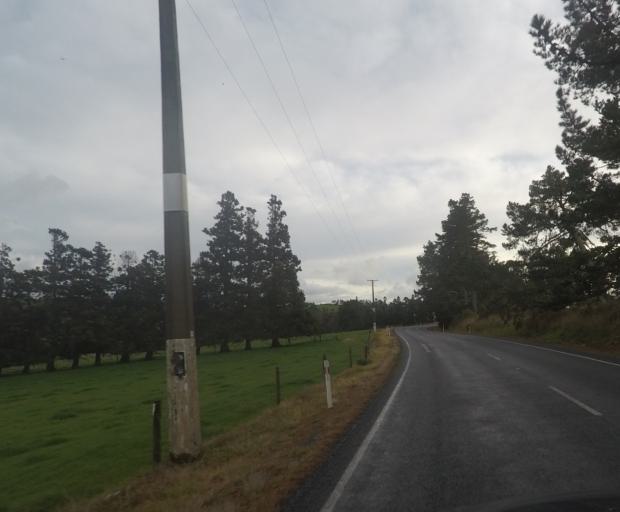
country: NZ
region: Auckland
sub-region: Auckland
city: Wellsford
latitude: -36.1858
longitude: 174.5802
